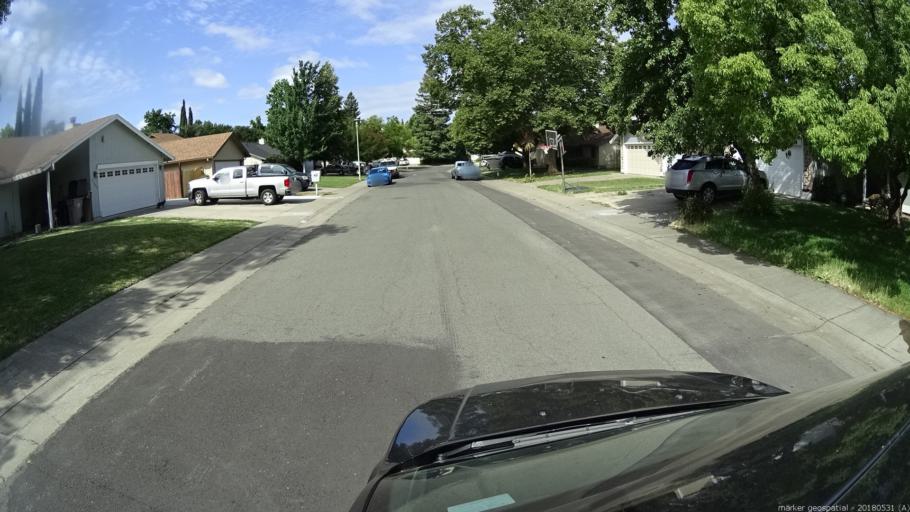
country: US
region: California
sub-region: Sacramento County
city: Sacramento
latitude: 38.6207
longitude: -121.4931
